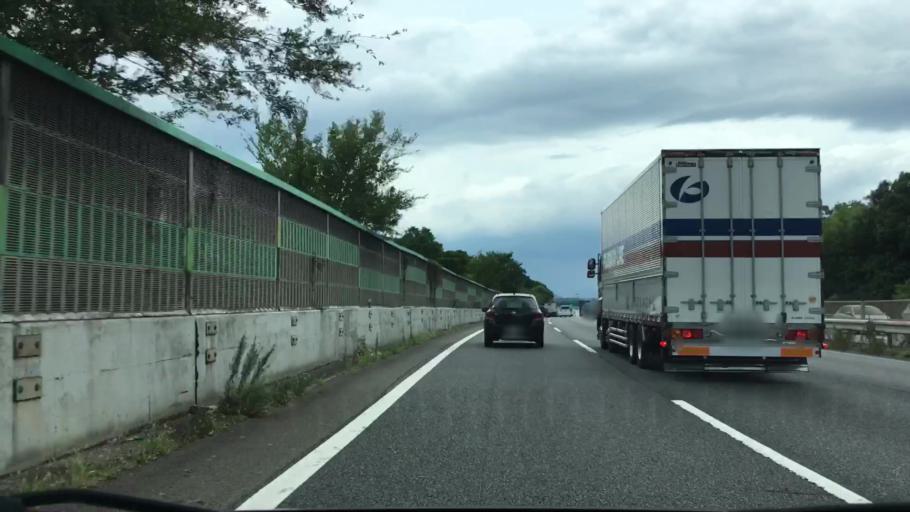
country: JP
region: Hyogo
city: Himeji
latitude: 34.8007
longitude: 134.7095
